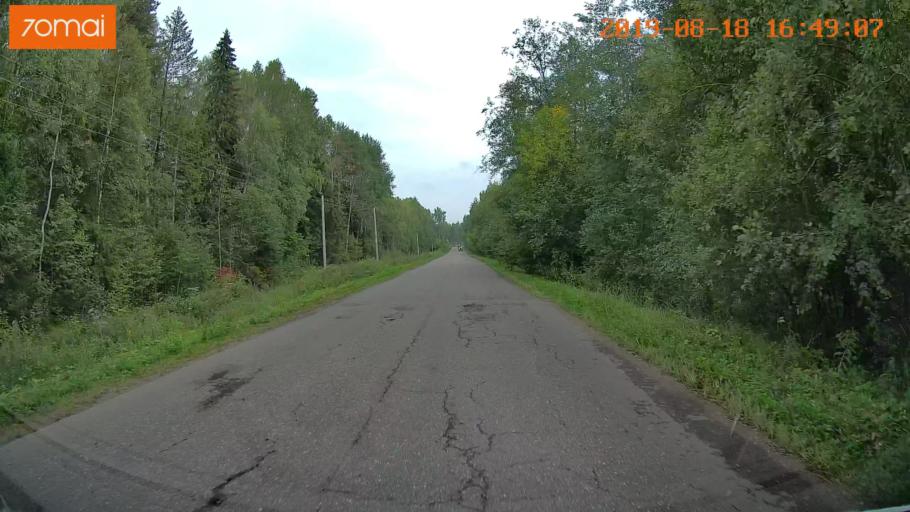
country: RU
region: Ivanovo
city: Novo-Talitsy
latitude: 57.0768
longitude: 40.8455
